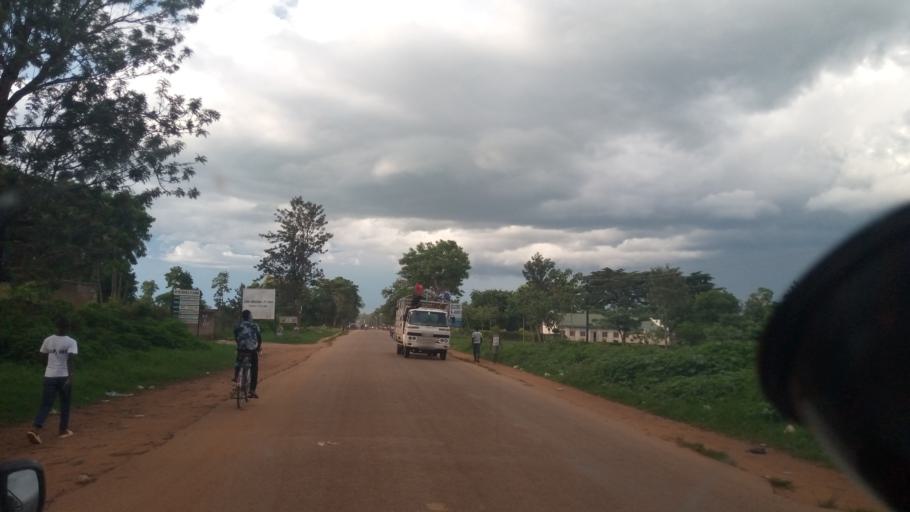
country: UG
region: Northern Region
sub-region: Lira District
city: Lira
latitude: 2.2582
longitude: 32.9072
